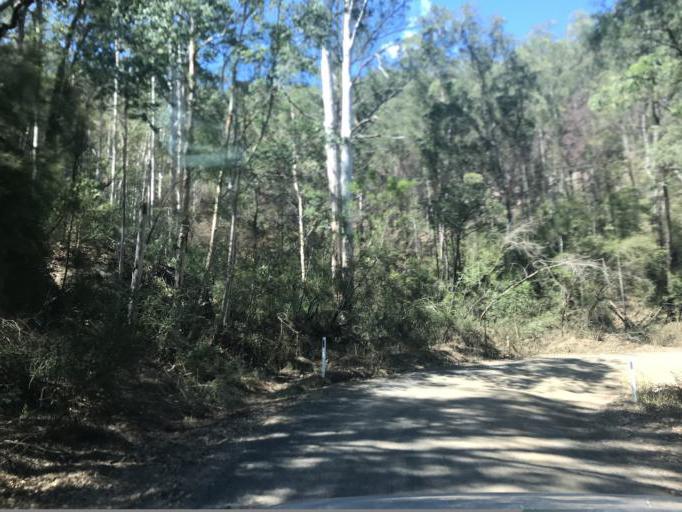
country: AU
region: New South Wales
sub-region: Wyong Shire
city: Little Jilliby
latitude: -33.1627
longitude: 151.0686
